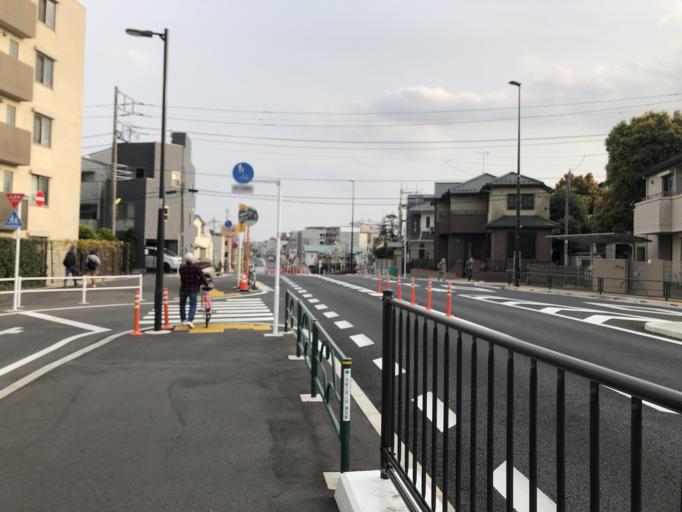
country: JP
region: Tokyo
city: Tokyo
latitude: 35.6443
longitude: 139.6423
